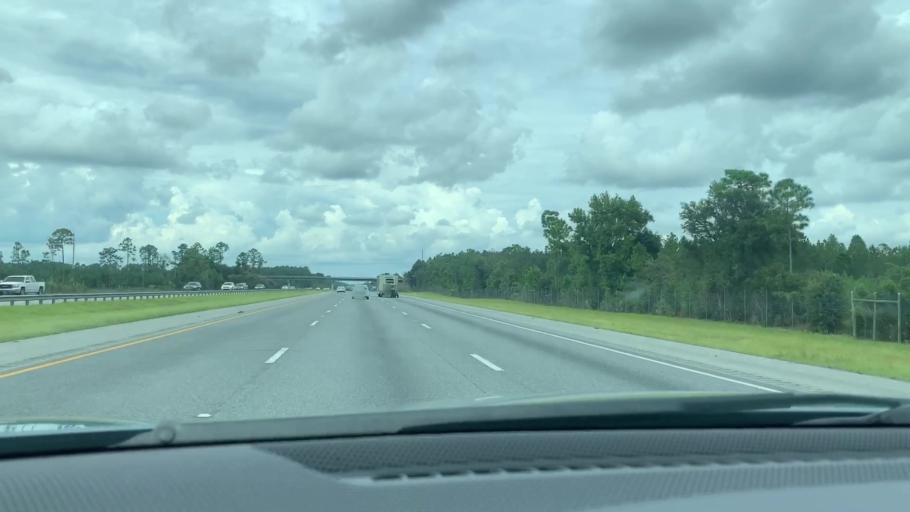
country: US
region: Georgia
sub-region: McIntosh County
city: Darien
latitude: 31.4279
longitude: -81.4432
